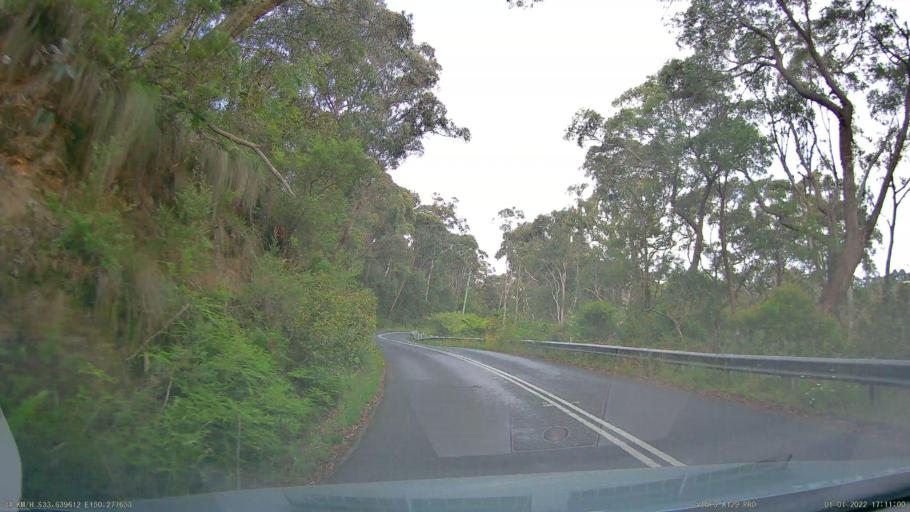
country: AU
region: New South Wales
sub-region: Blue Mountains Municipality
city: Blackheath
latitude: -33.6396
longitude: 150.2777
